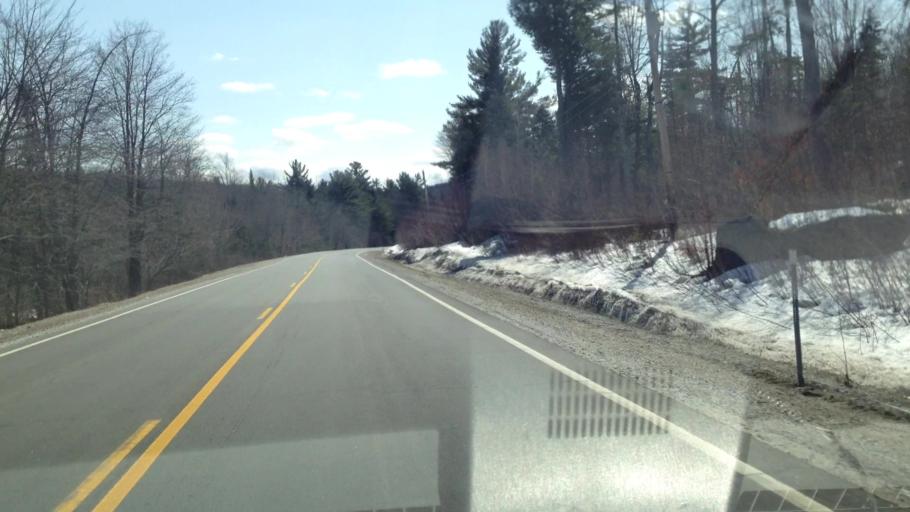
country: US
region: New Hampshire
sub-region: Merrimack County
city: Wilmot
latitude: 43.4745
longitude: -71.9648
